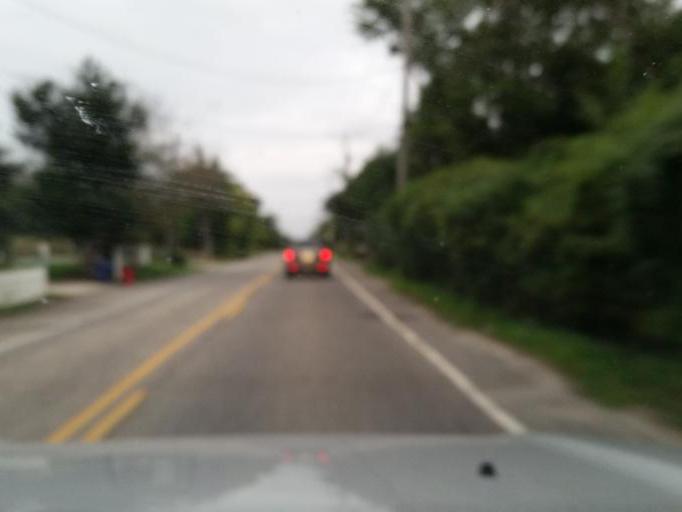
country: US
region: New Jersey
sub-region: Cape May County
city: West Cape May
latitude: 38.9399
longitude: -74.9509
